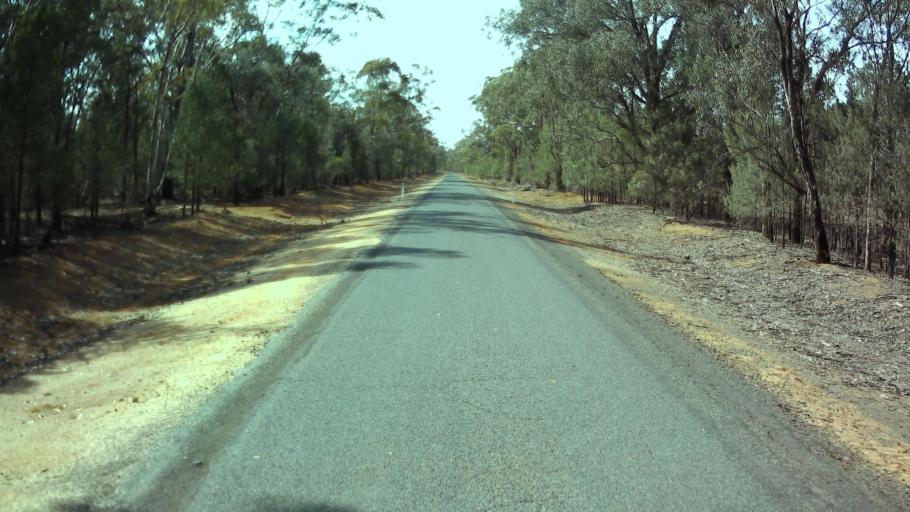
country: AU
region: New South Wales
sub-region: Weddin
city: Grenfell
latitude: -33.7190
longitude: 148.0272
